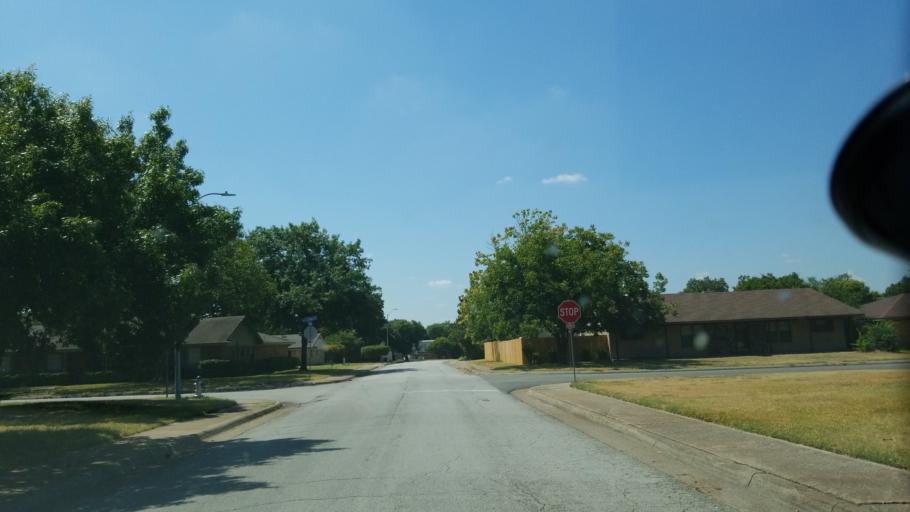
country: US
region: Texas
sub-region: Dallas County
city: Duncanville
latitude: 32.6545
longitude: -96.8952
